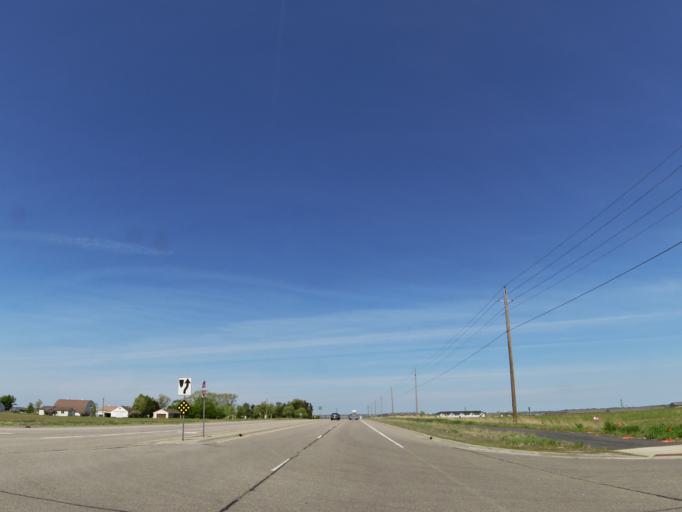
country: US
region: Minnesota
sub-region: Scott County
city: Shakopee
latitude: 44.7676
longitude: -93.4700
